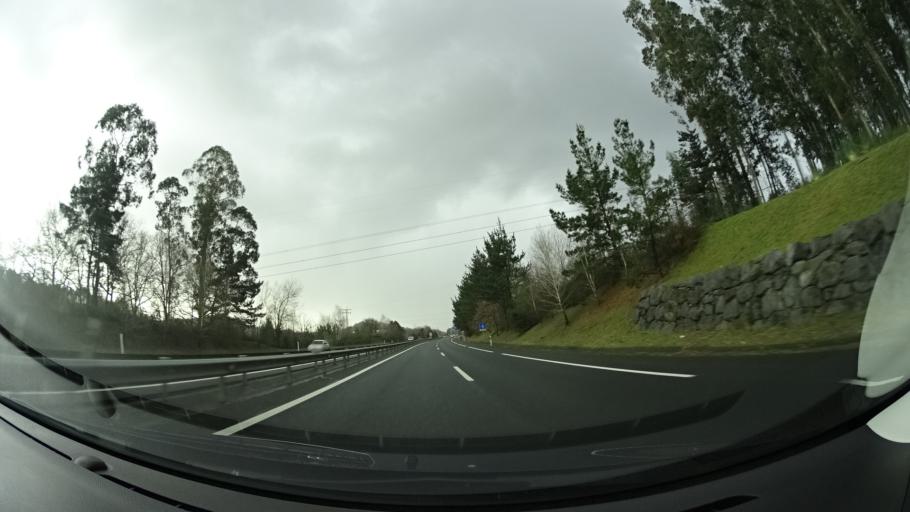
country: ES
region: Basque Country
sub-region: Bizkaia
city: Gatika
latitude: 43.3464
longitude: -2.8611
